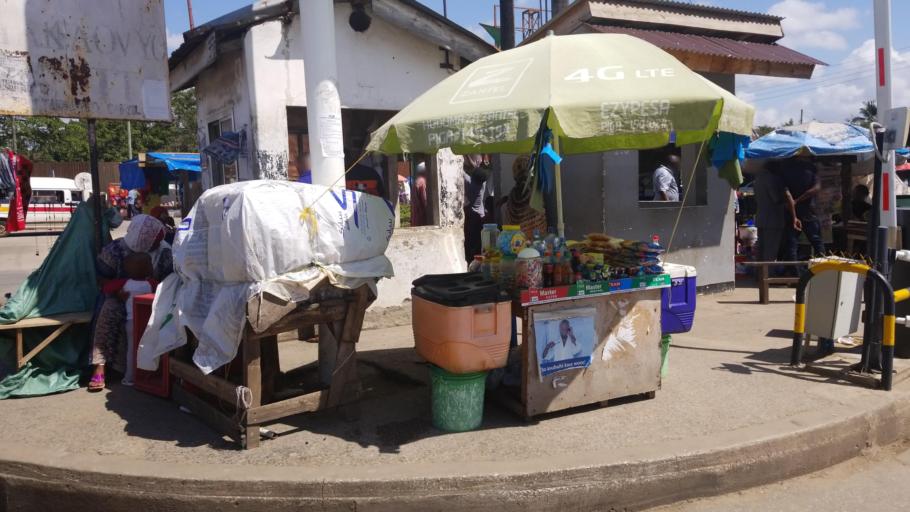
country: TZ
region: Tanga
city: Tanga
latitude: -5.0802
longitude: 39.0984
